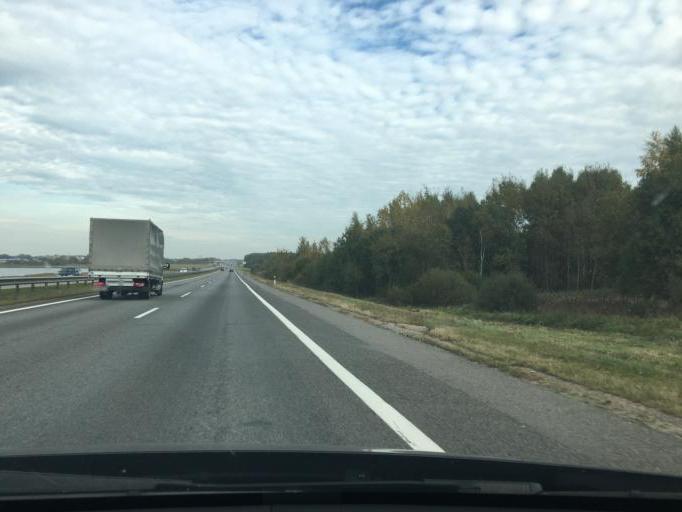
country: BY
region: Minsk
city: Dzyarzhynsk
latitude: 53.6677
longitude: 27.1585
